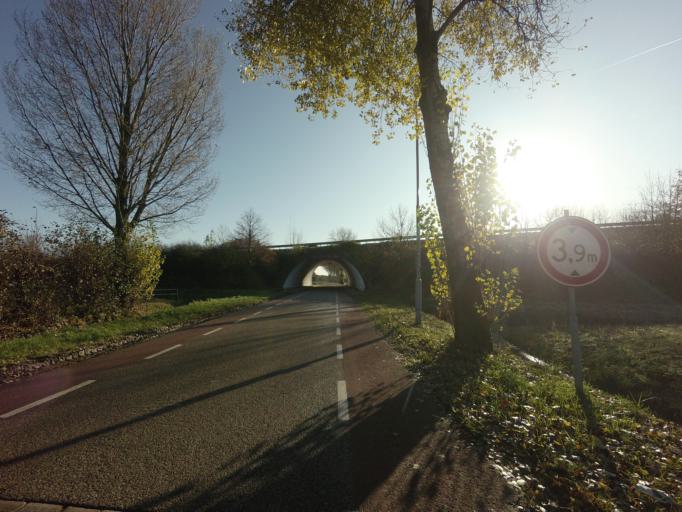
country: NL
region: Gelderland
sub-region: Gemeente Zaltbommel
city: Zaltbommel
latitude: 51.7942
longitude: 5.2681
